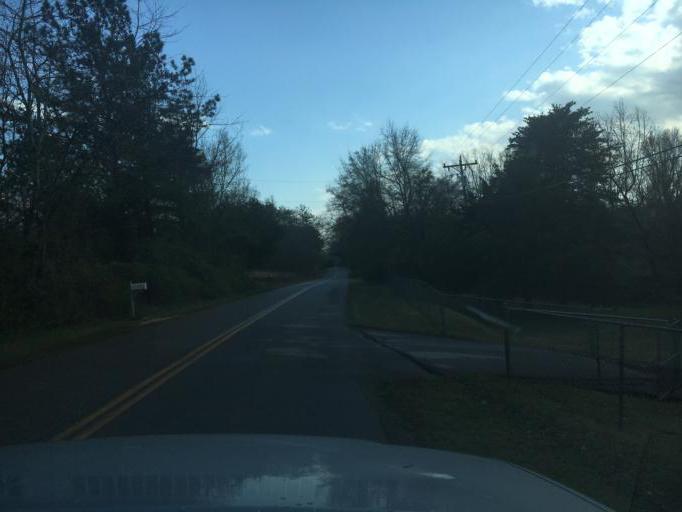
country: US
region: South Carolina
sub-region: Greenville County
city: Parker
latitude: 34.8608
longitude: -82.5019
